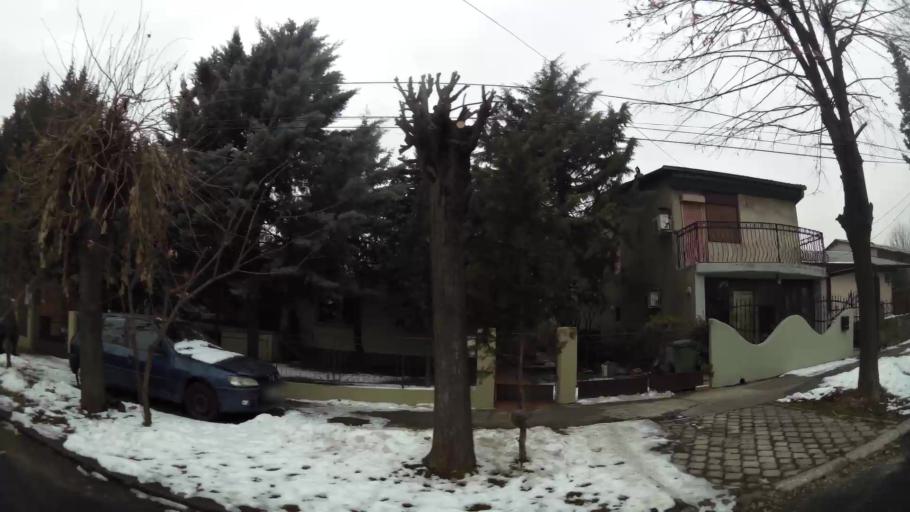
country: MK
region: Cair
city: Cair
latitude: 42.0149
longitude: 21.4603
